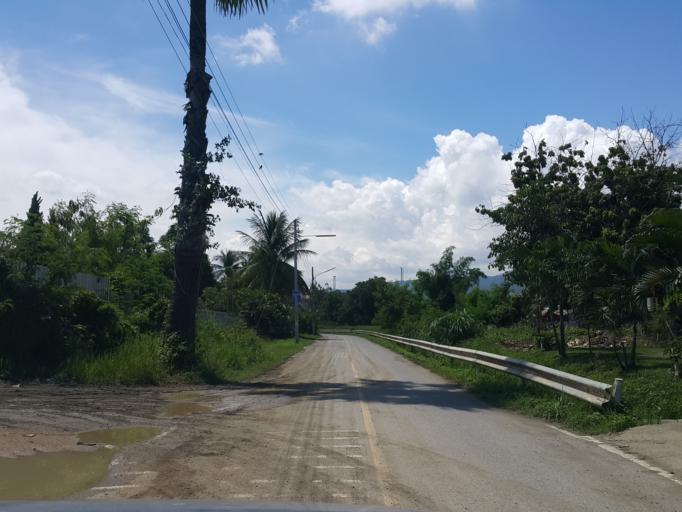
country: TH
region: Chiang Mai
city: Chiang Mai
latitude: 18.7467
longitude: 98.9502
